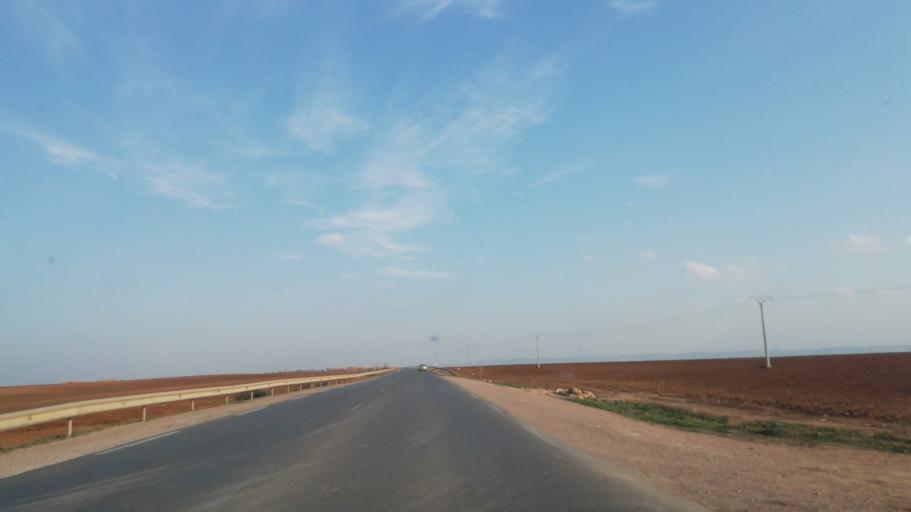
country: DZ
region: Relizane
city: Relizane
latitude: 35.8923
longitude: 0.6173
